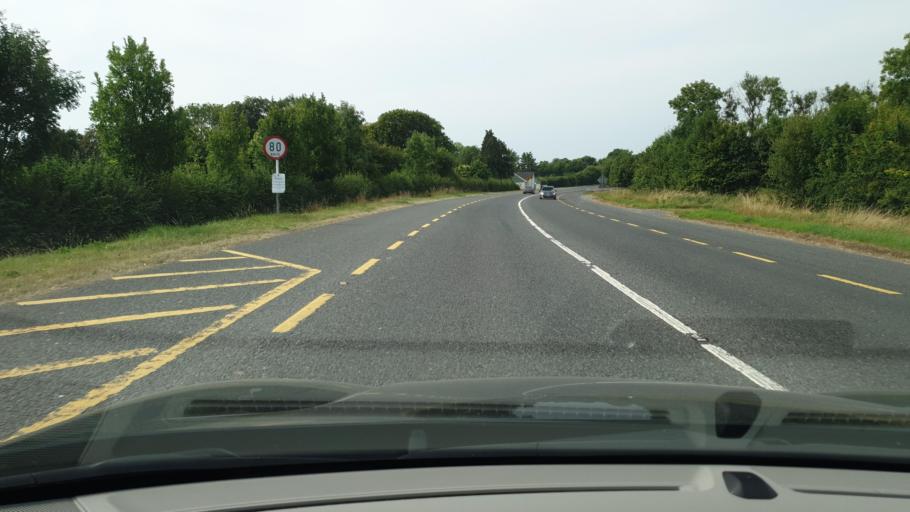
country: IE
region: Leinster
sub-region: An Mhi
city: Navan
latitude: 53.6324
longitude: -6.7463
